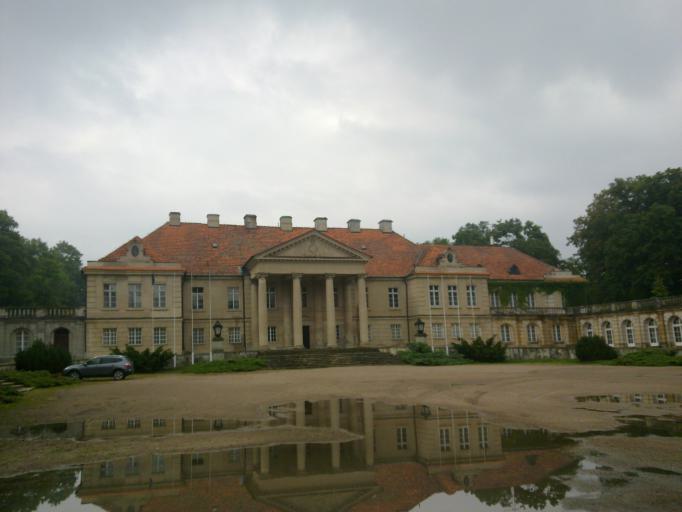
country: PL
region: Greater Poland Voivodeship
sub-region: Powiat gnieznienski
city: Czerniejewo
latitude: 52.4335
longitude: 17.4889
